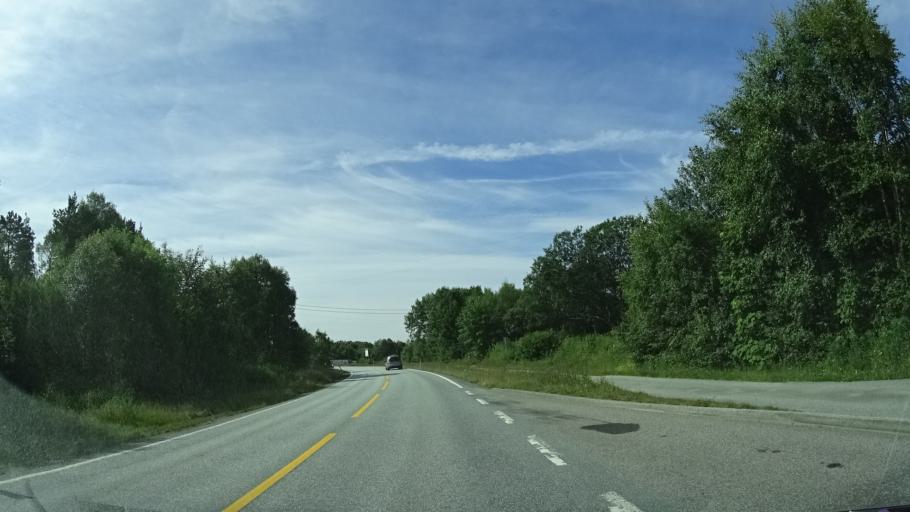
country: NO
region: Hordaland
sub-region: Bomlo
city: Mosterhamn
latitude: 59.6725
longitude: 5.4596
